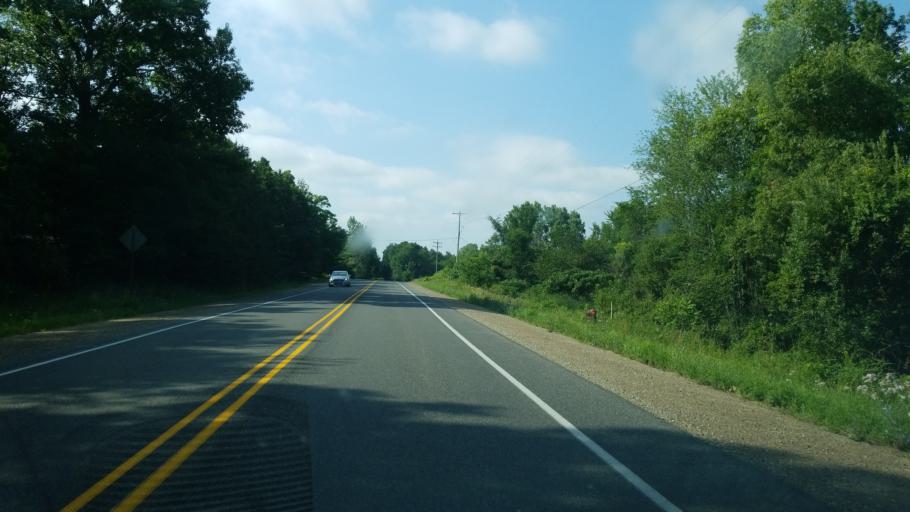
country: US
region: Michigan
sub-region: Kent County
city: Comstock Park
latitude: 43.0852
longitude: -85.6515
